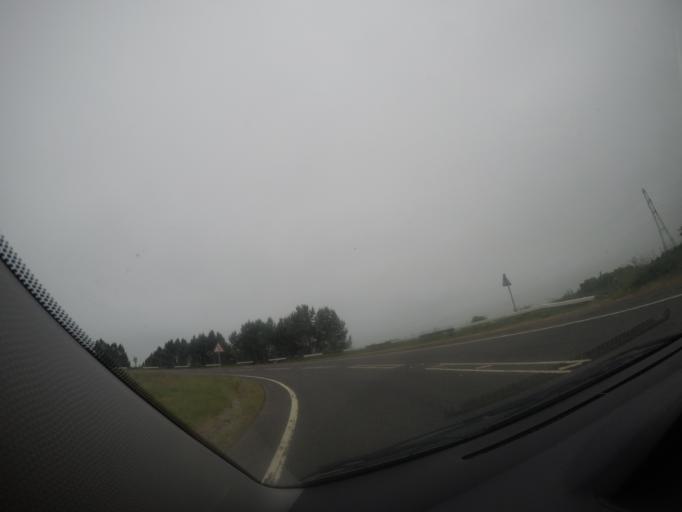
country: GB
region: Scotland
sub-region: Angus
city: Brechin
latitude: 56.7302
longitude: -2.6986
